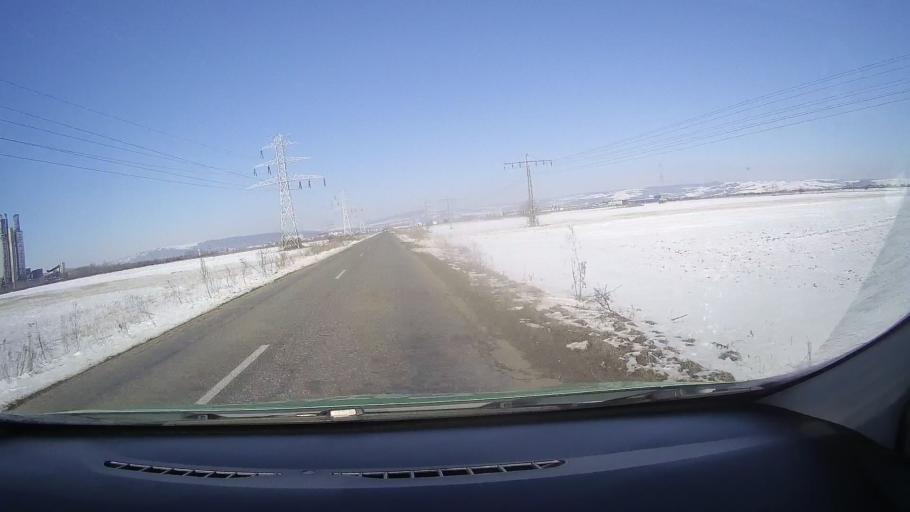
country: RO
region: Brasov
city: Fogarasch
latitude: 45.8116
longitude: 24.9892
